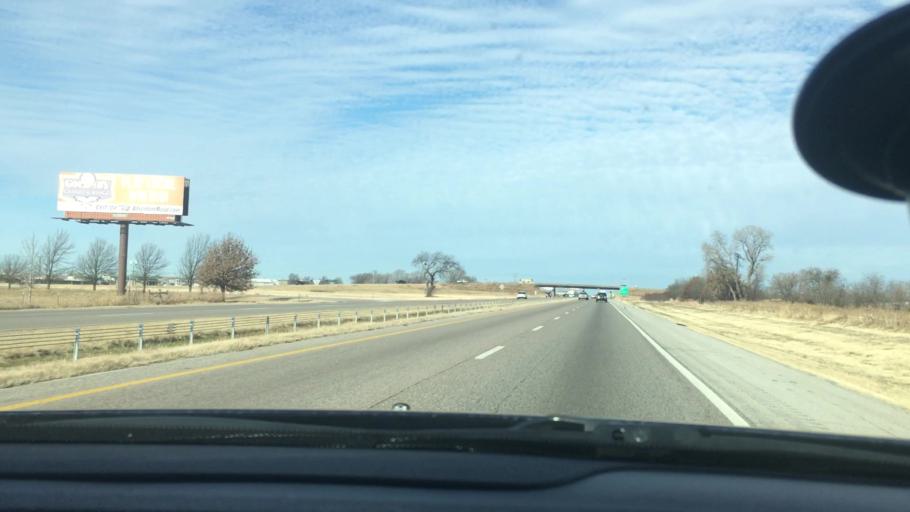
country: US
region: Oklahoma
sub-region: McClain County
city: Goldsby
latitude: 35.1495
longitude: -97.4733
